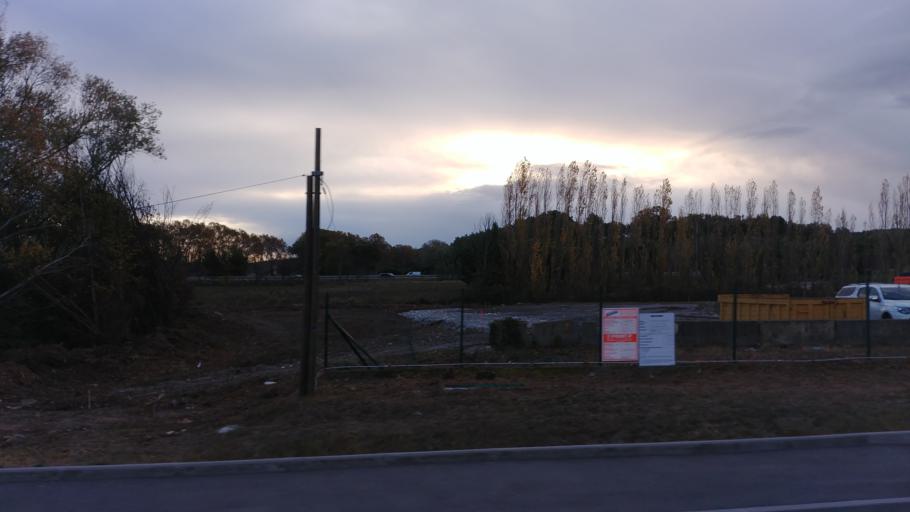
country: FR
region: Provence-Alpes-Cote d'Azur
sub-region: Departement des Bouches-du-Rhone
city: Venelles
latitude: 43.5840
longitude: 5.4738
